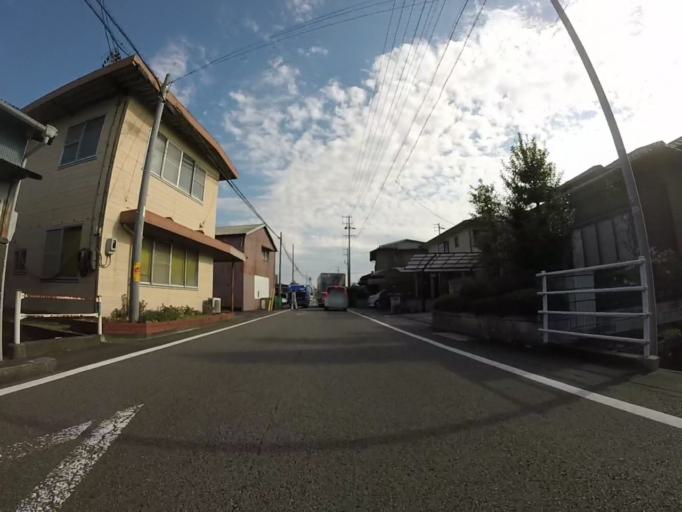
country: JP
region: Shizuoka
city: Shimada
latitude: 34.7817
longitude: 138.2358
